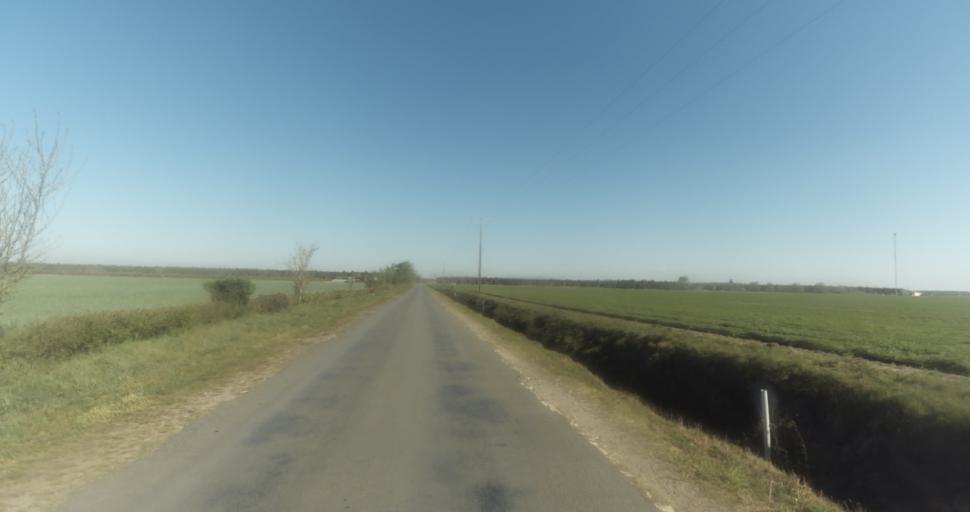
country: FR
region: Aquitaine
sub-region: Departement de la Gironde
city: Marcheprime
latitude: 44.7712
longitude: -0.8570
